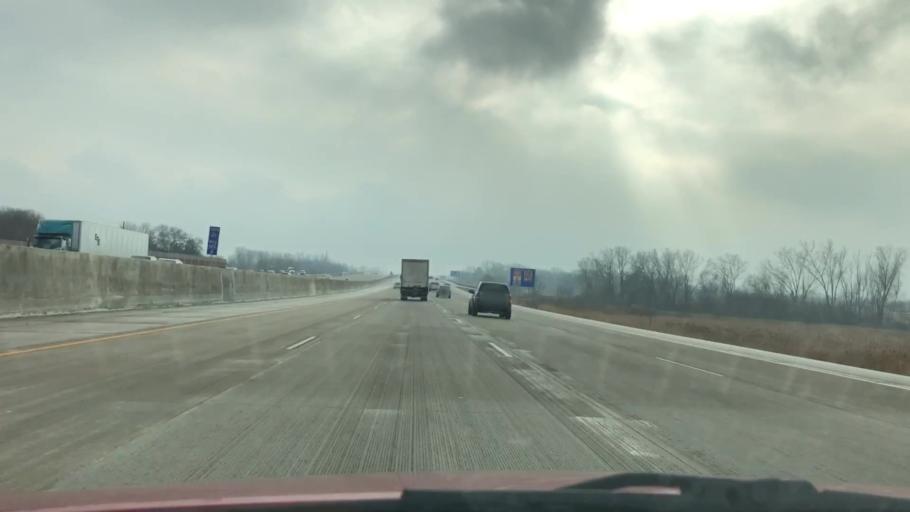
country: US
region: Wisconsin
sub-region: Brown County
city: Ashwaubenon
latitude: 44.4896
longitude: -88.0811
